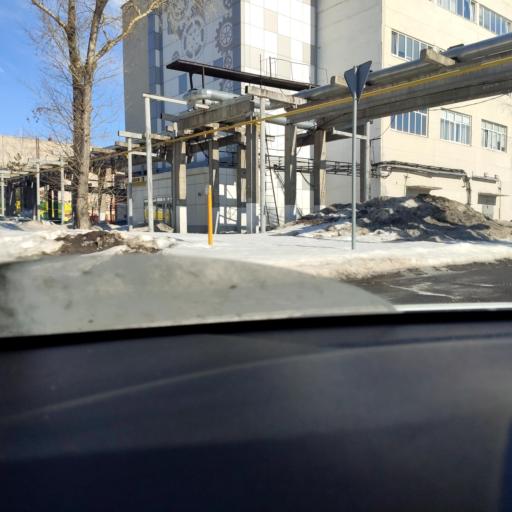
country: RU
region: Tatarstan
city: Staroye Arakchino
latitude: 55.8354
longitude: 49.0378
